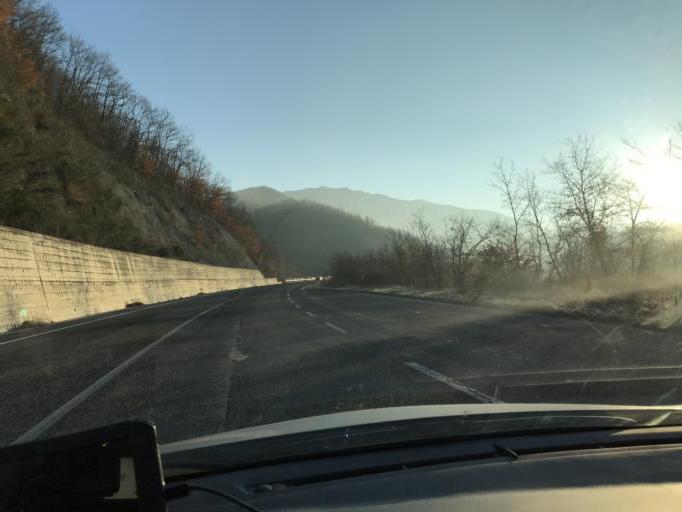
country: IT
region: Latium
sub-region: Provincia di Rieti
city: Concerviano
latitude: 42.3357
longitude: 13.0001
